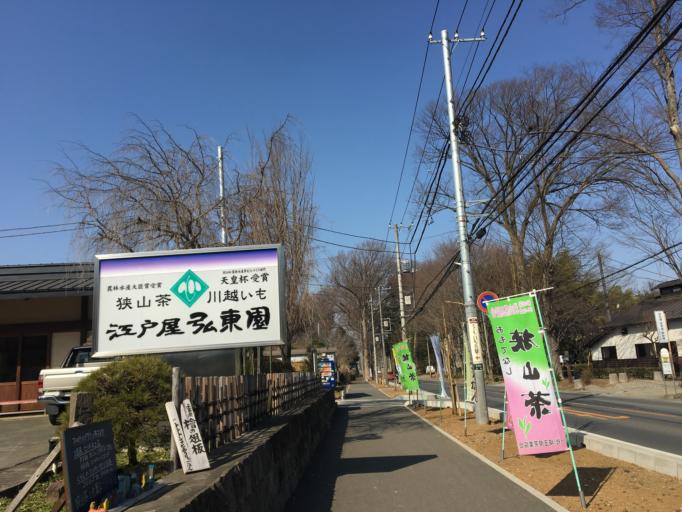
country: JP
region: Saitama
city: Oi
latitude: 35.8331
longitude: 139.5009
